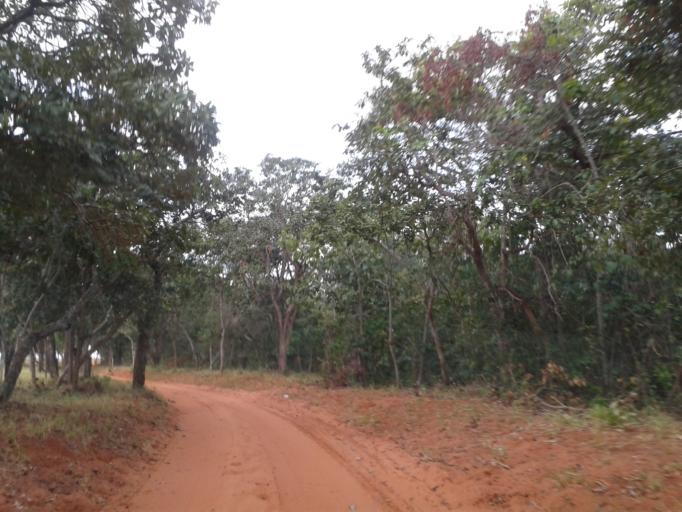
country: BR
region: Minas Gerais
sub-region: Campina Verde
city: Campina Verde
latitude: -19.4475
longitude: -49.6204
